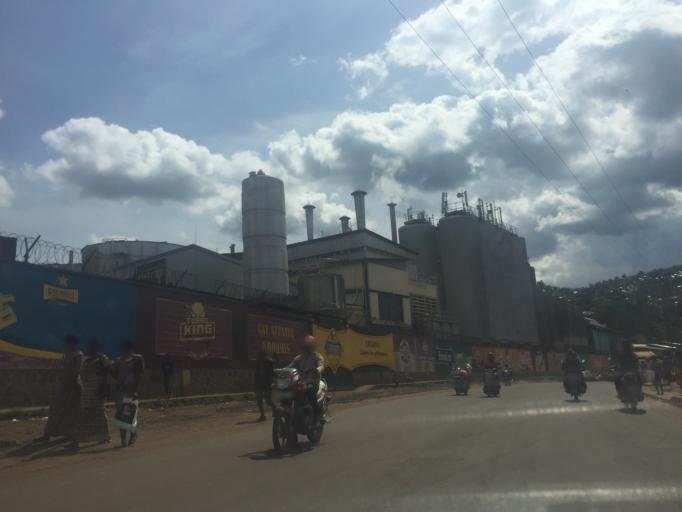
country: CD
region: South Kivu
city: Bukavu
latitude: -2.4840
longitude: 28.8440
